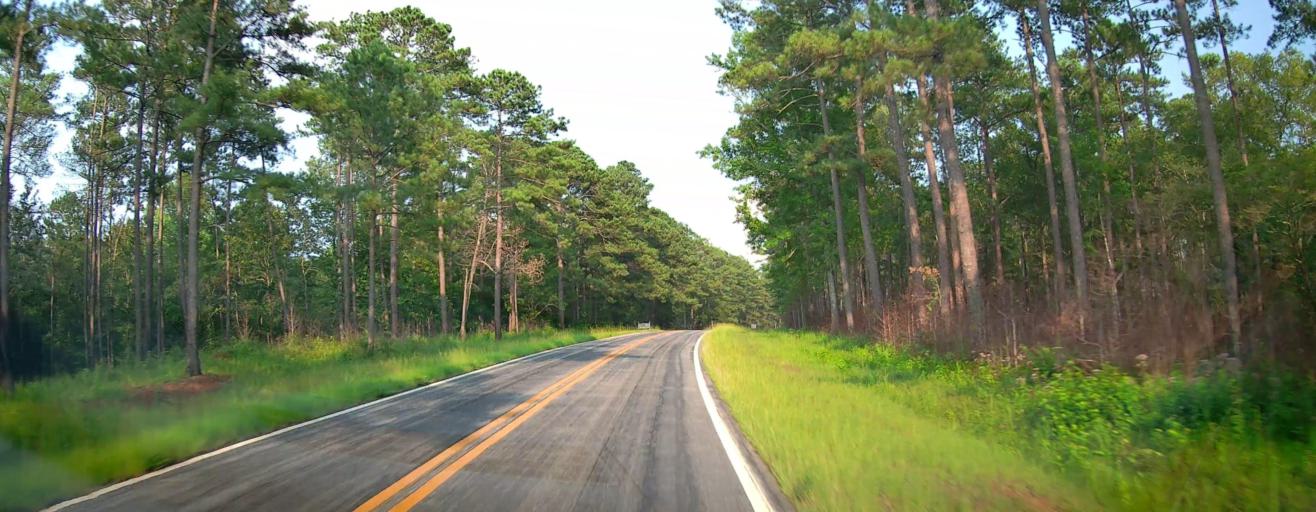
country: US
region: Georgia
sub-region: Jones County
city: Gray
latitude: 33.0991
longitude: -83.7171
